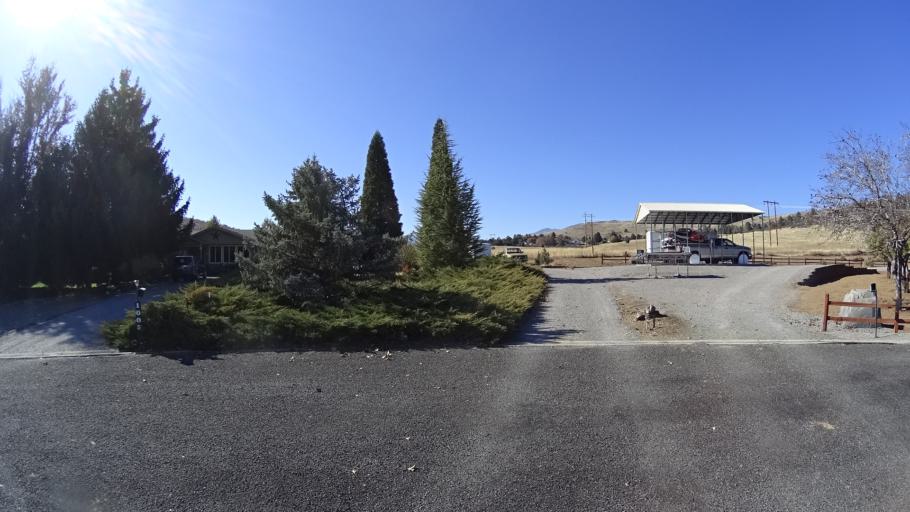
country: US
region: California
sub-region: Siskiyou County
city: Yreka
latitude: 41.7432
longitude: -122.6038
